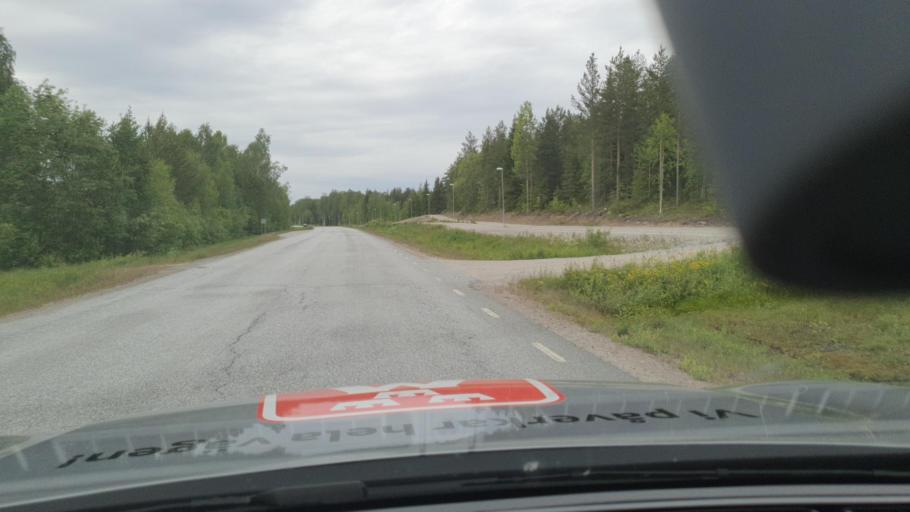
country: SE
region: Norrbotten
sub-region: Kalix Kommun
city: Rolfs
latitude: 65.8736
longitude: 23.1091
